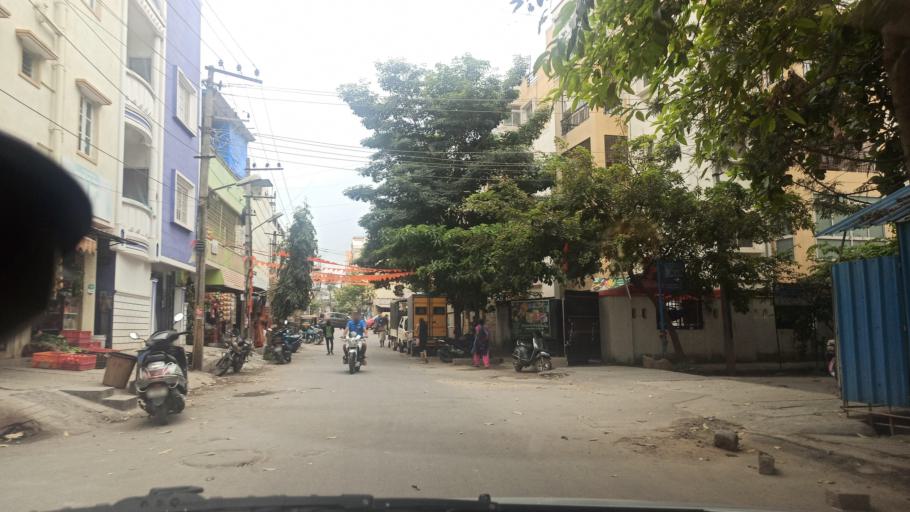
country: IN
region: Karnataka
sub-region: Bangalore Urban
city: Bangalore
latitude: 13.0357
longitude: 77.6014
